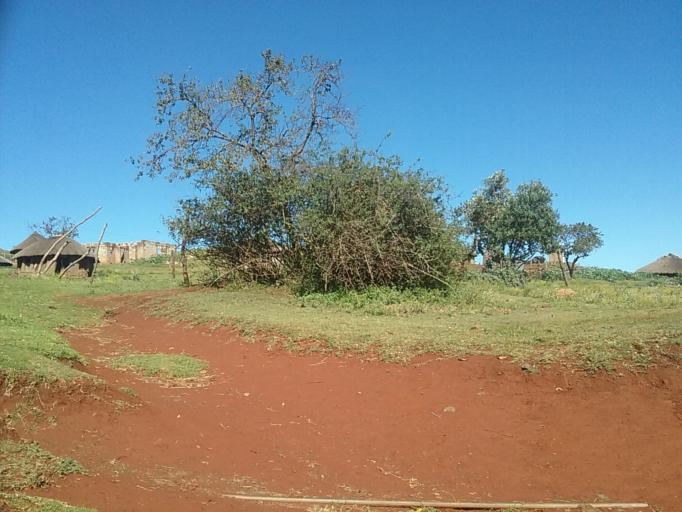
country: LS
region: Berea
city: Teyateyaneng
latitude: -29.2199
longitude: 27.9410
